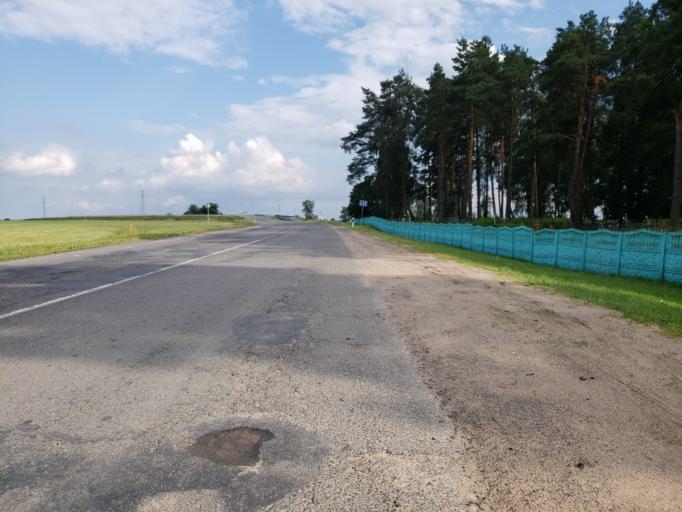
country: BY
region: Minsk
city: Chervyen'
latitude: 53.7275
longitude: 28.3904
